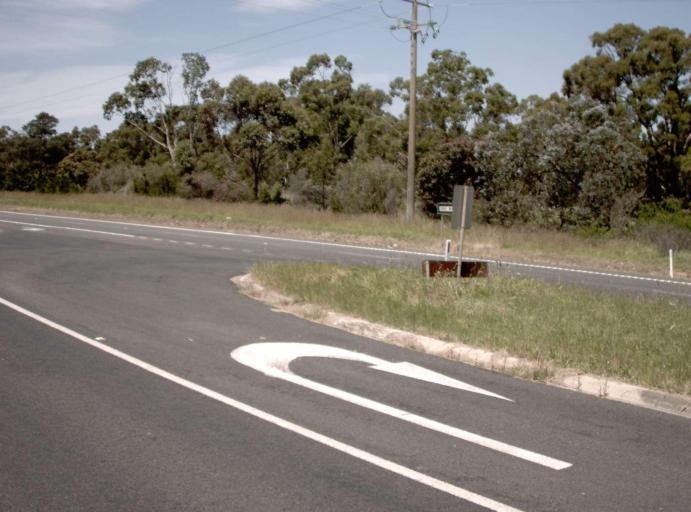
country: AU
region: Victoria
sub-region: Latrobe
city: Traralgon
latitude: -38.2072
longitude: 146.5023
